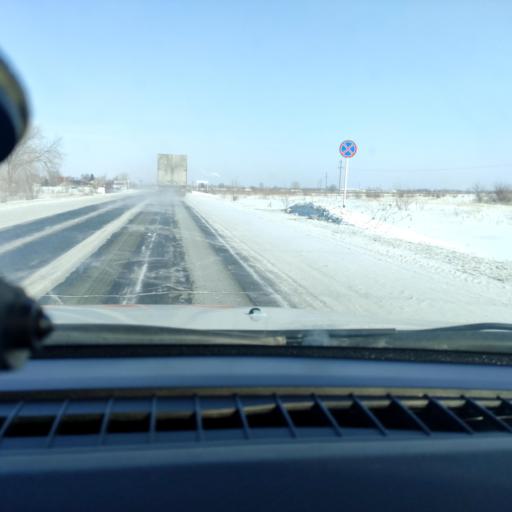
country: RU
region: Samara
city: Smyshlyayevka
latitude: 53.1757
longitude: 50.4595
